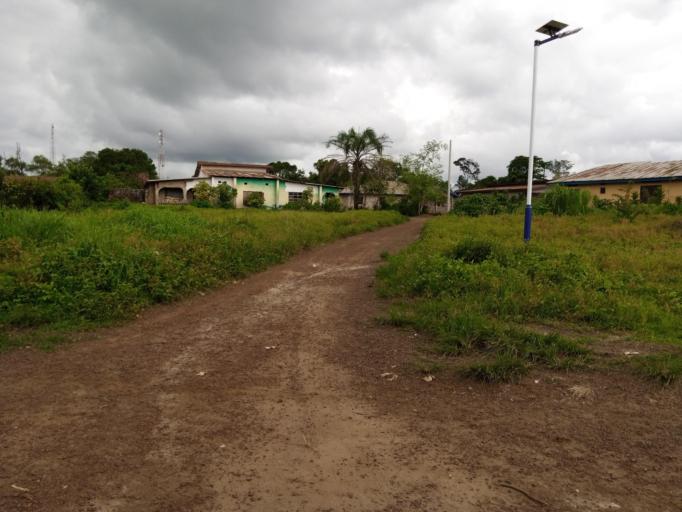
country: SL
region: Southern Province
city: Moyamba
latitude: 8.1649
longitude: -12.4261
